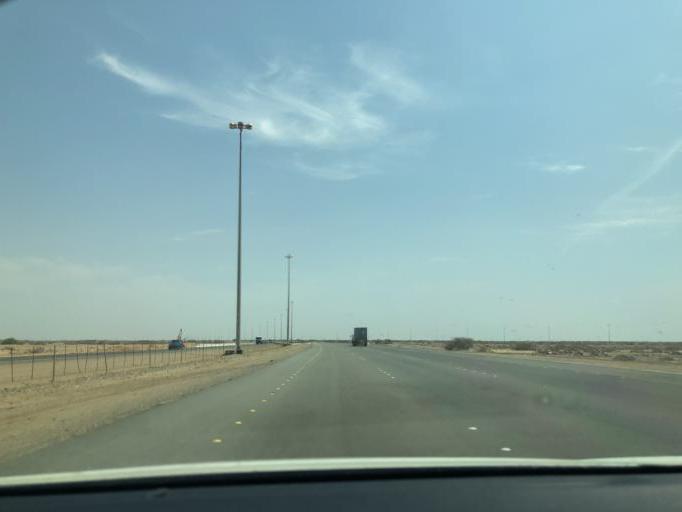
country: SA
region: Makkah
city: Rabigh
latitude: 22.2477
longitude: 39.1147
